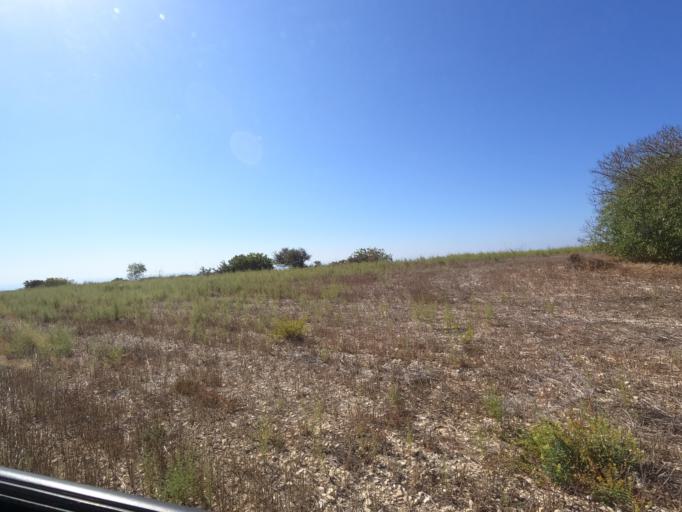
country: CY
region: Pafos
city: Mesogi
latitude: 34.8099
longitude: 32.4901
